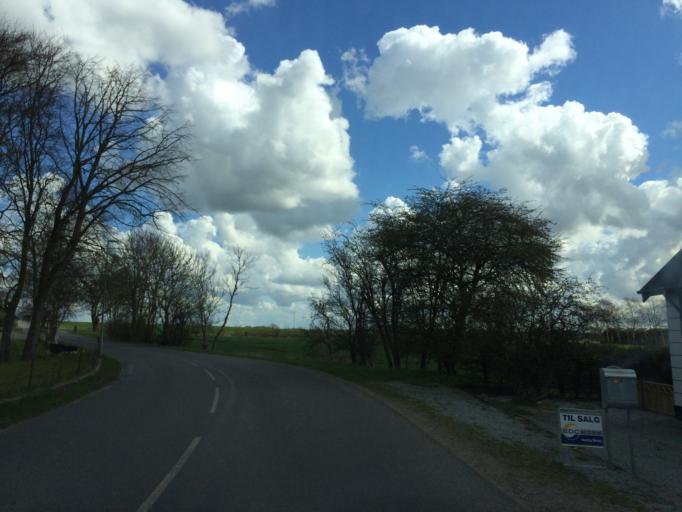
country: DK
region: South Denmark
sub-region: Odense Kommune
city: Bellinge
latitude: 55.2527
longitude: 10.2751
